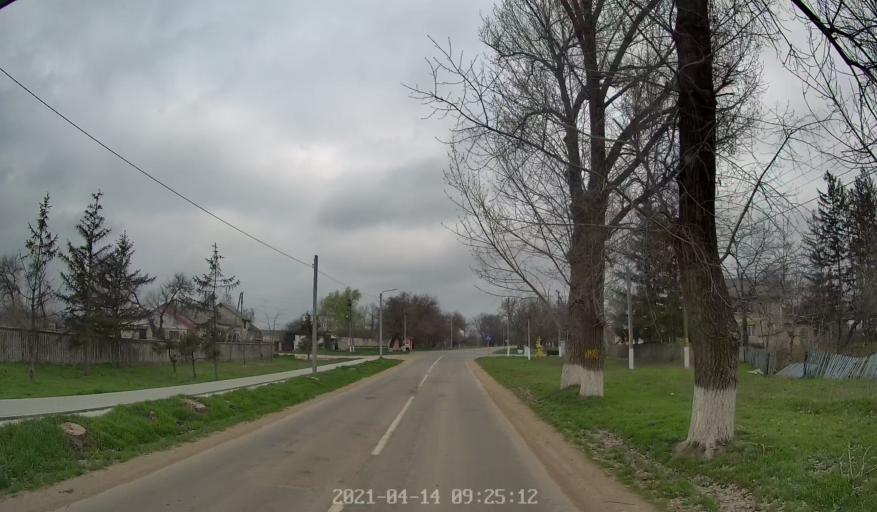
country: MD
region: Chisinau
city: Vadul lui Voda
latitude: 47.1140
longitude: 29.1113
